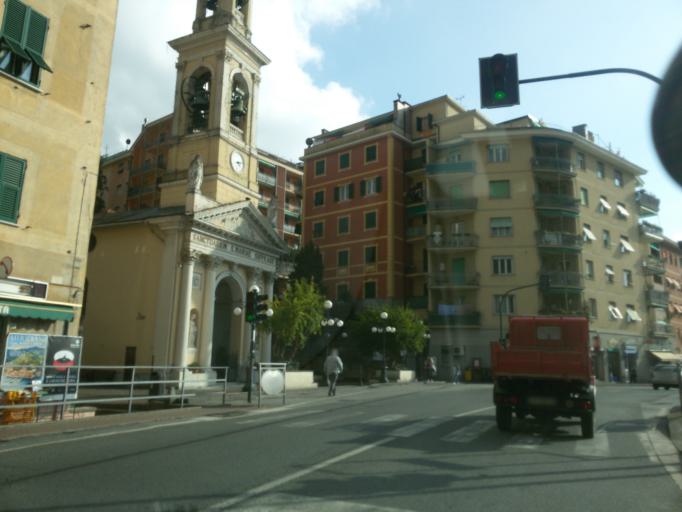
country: IT
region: Liguria
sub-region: Provincia di Genova
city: Recco
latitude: 44.3649
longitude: 9.1468
